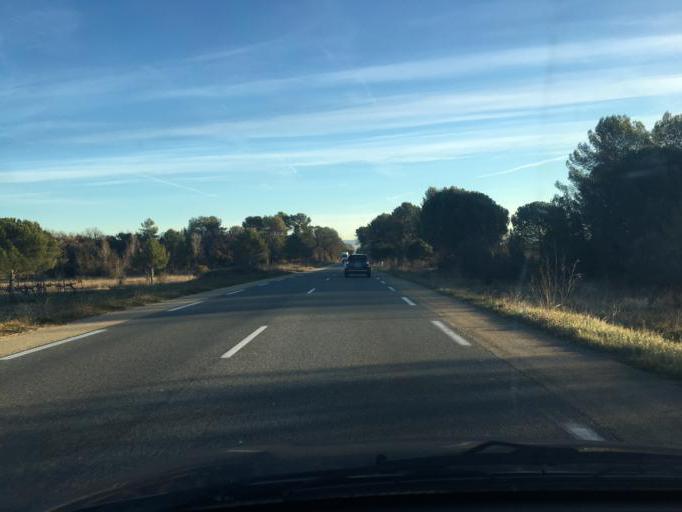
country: FR
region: Provence-Alpes-Cote d'Azur
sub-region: Departement du Var
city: La Motte
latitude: 43.4584
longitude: 6.5204
